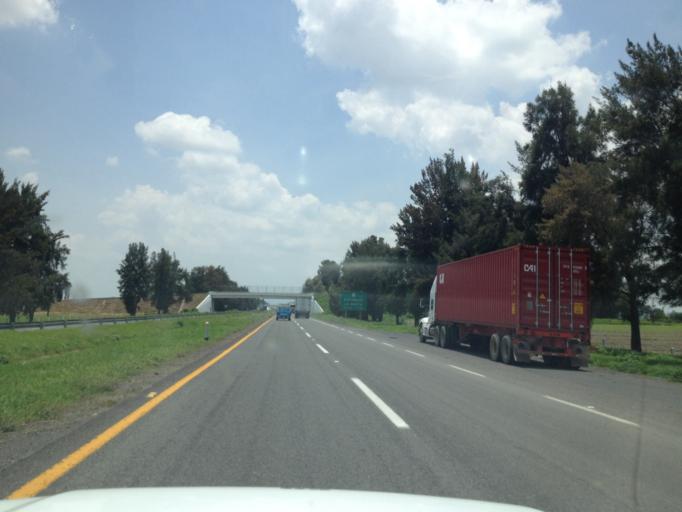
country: MX
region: Jalisco
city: La Barca
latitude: 20.3220
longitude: -102.5131
